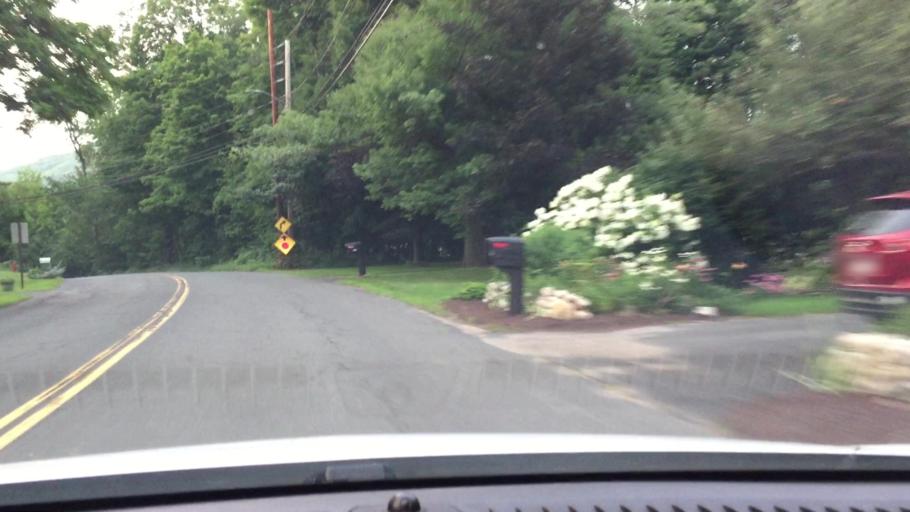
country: US
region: Massachusetts
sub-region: Hampden County
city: Westfield
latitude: 42.1464
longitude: -72.8135
